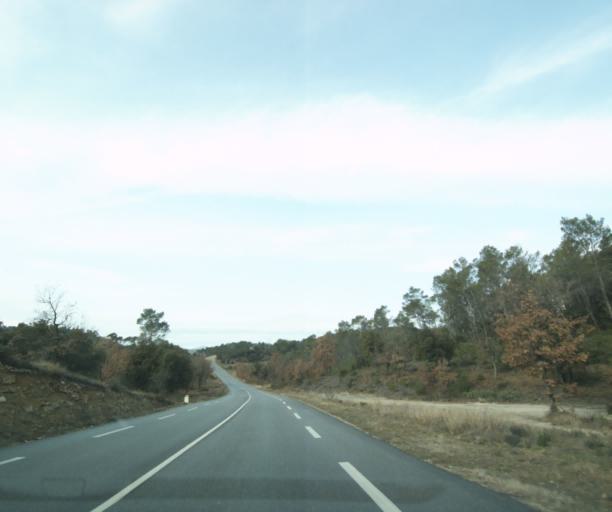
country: FR
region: Provence-Alpes-Cote d'Azur
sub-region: Departement du Var
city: Tourves
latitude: 43.4014
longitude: 5.9605
